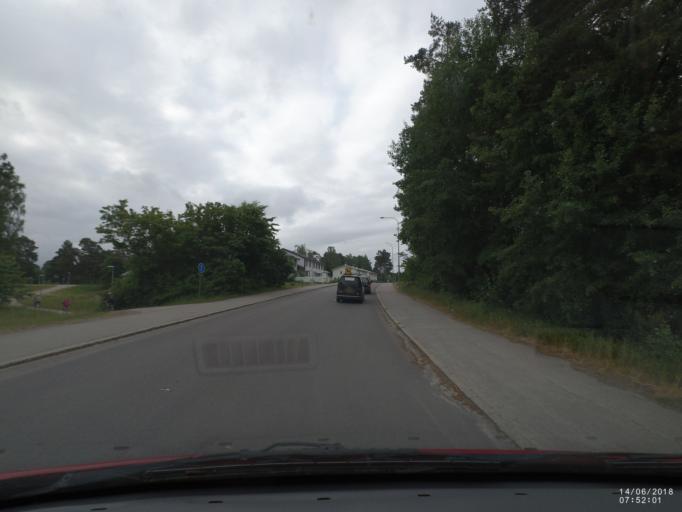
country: SE
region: Soedermanland
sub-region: Nykopings Kommun
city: Nykoping
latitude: 58.7646
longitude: 17.0218
